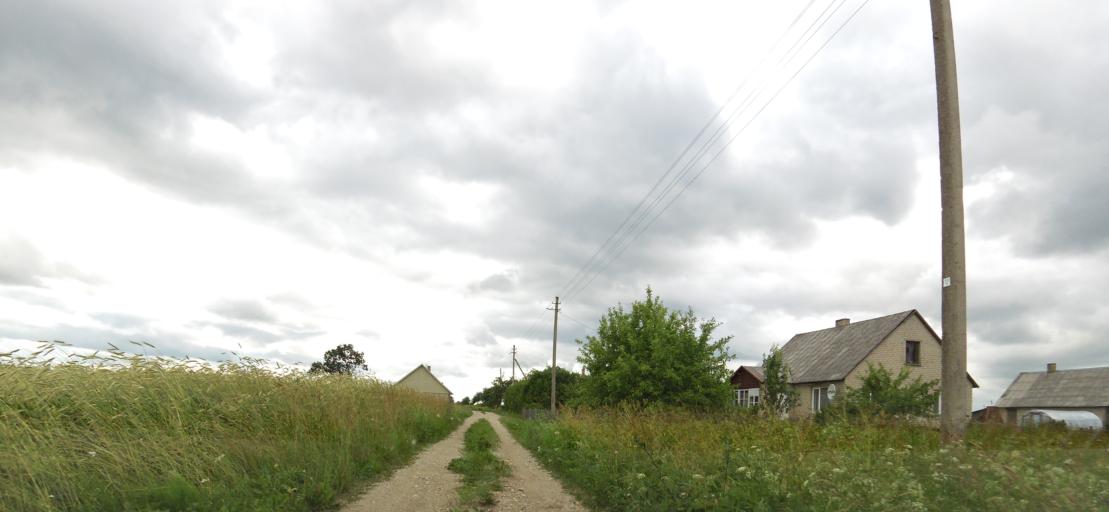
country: LT
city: Obeliai
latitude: 56.0702
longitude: 25.1077
